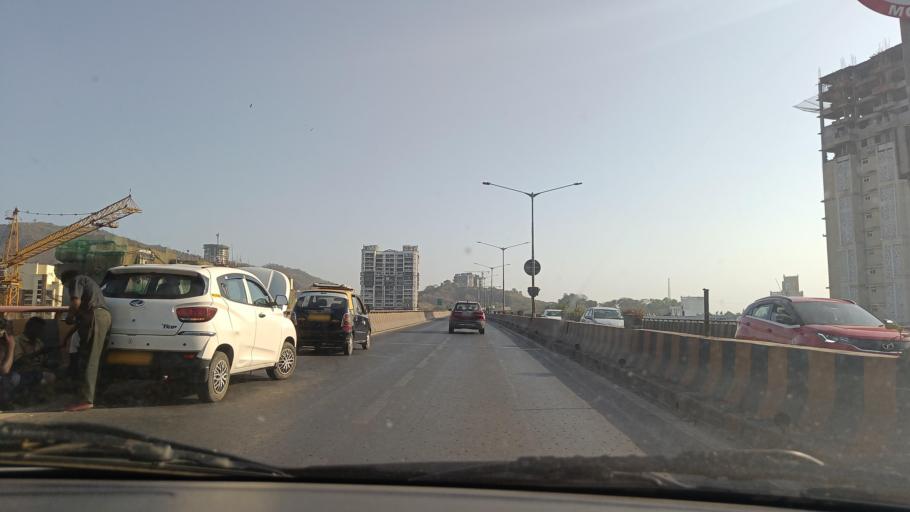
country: IN
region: Maharashtra
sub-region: Mumbai Suburban
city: Mumbai
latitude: 19.0487
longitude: 72.9100
